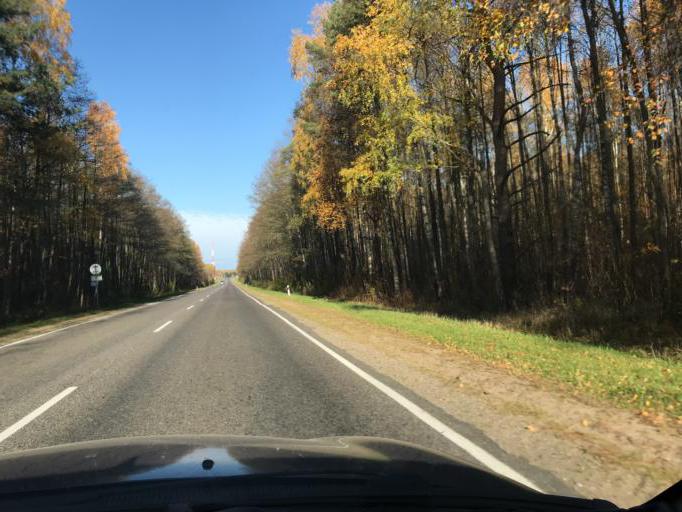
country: BY
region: Grodnenskaya
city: Lida
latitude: 53.9881
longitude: 25.2184
